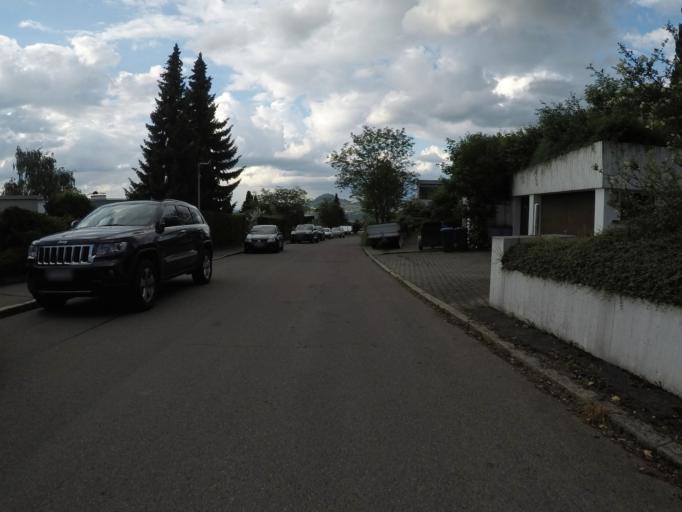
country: DE
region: Baden-Wuerttemberg
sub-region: Tuebingen Region
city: Pfullingen
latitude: 48.4487
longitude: 9.2181
